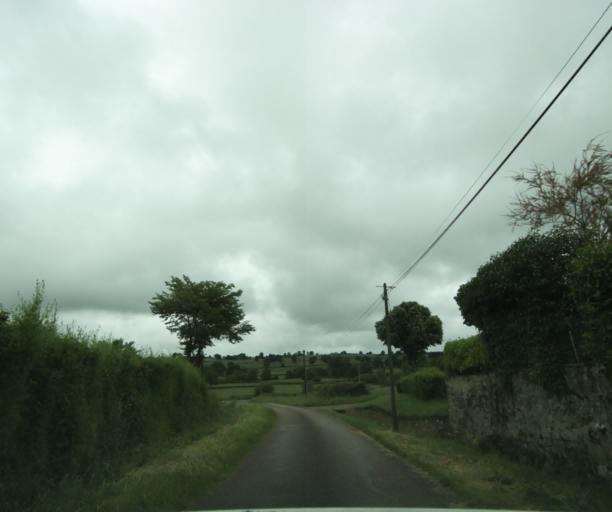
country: FR
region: Bourgogne
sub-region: Departement de Saone-et-Loire
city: Charolles
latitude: 46.4611
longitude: 4.3128
